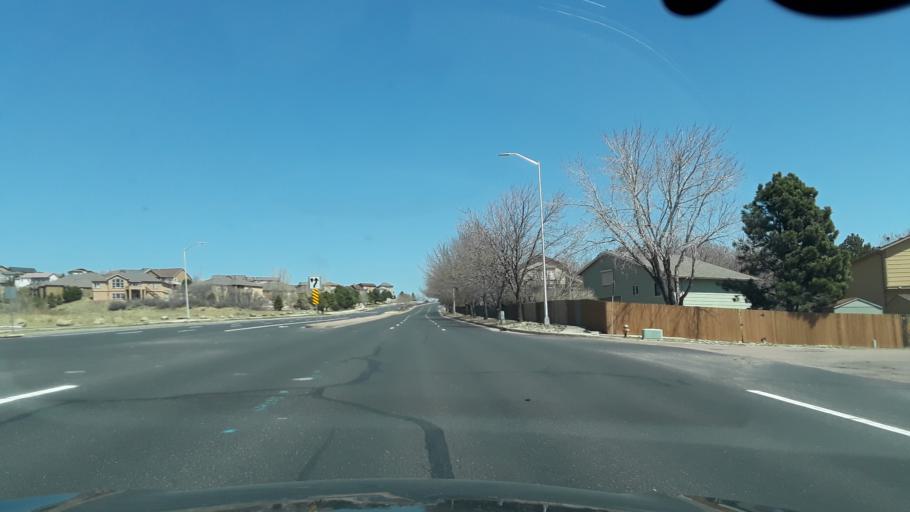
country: US
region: Colorado
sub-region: El Paso County
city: Cimarron Hills
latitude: 38.9079
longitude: -104.7370
